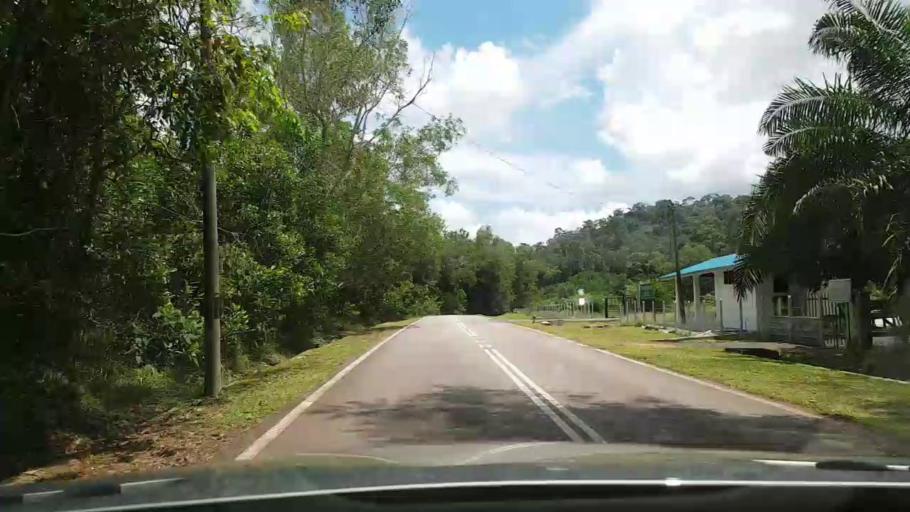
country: MY
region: Pahang
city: Pekan
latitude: 3.1549
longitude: 102.9721
